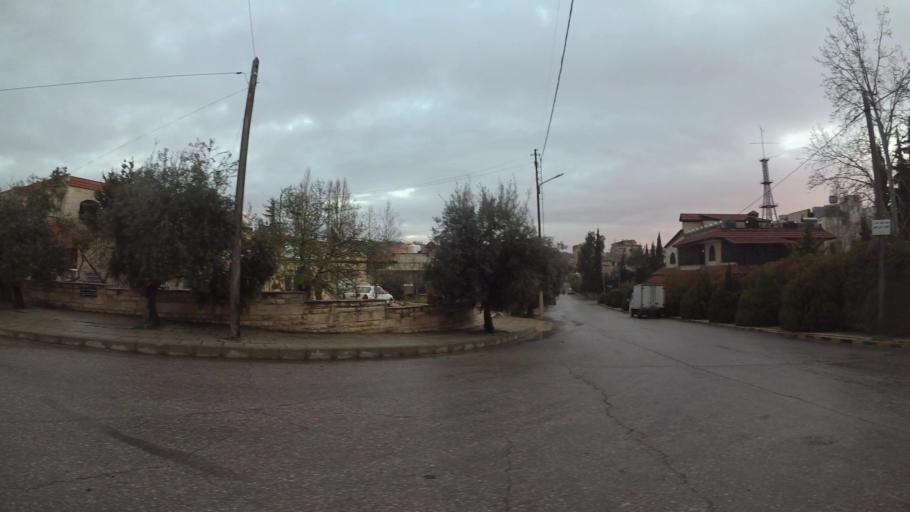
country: JO
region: Amman
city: Al Jubayhah
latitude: 32.0323
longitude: 35.8186
